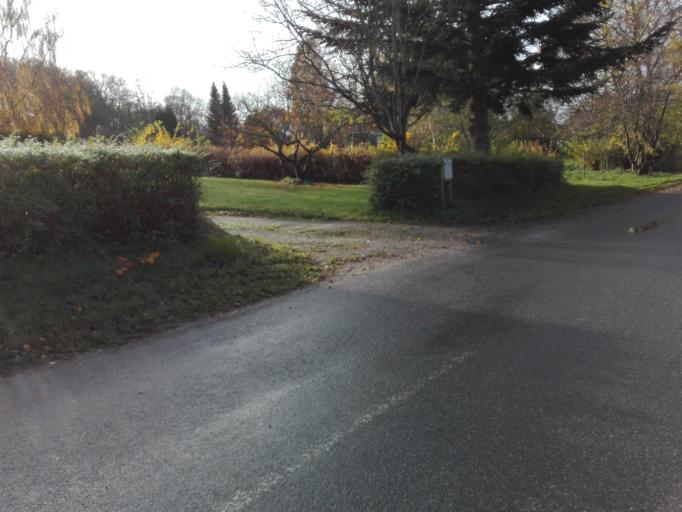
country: DK
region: Central Jutland
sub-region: Arhus Kommune
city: Beder
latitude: 56.0740
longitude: 10.2250
